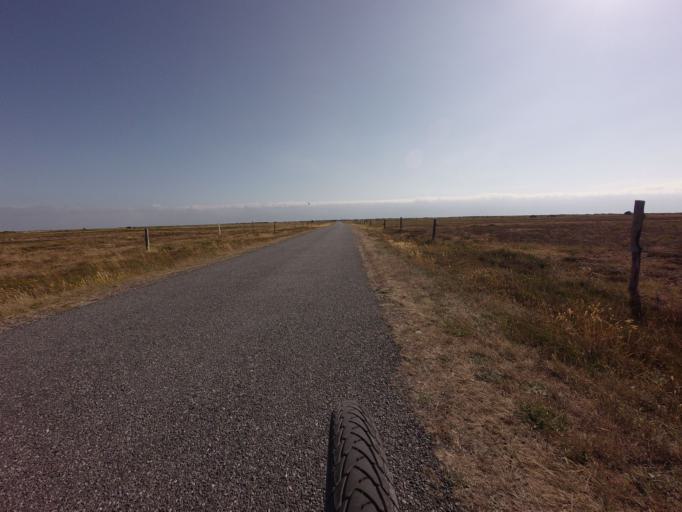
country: DK
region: North Denmark
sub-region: Laeso Kommune
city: Byrum
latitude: 57.2540
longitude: 10.8808
